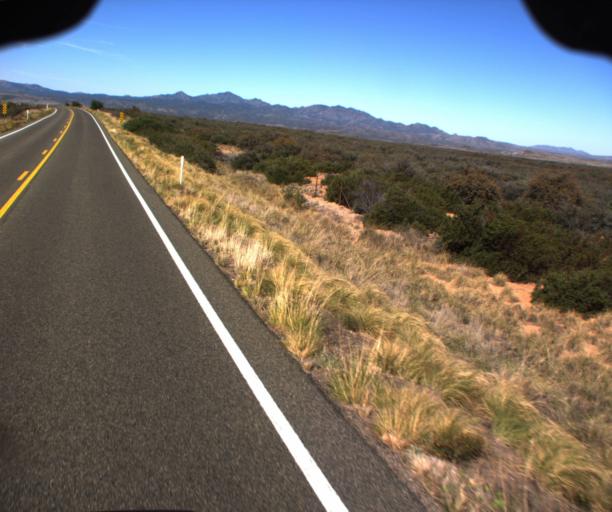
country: US
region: Arizona
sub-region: Yavapai County
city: Prescott
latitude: 34.4057
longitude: -112.6188
